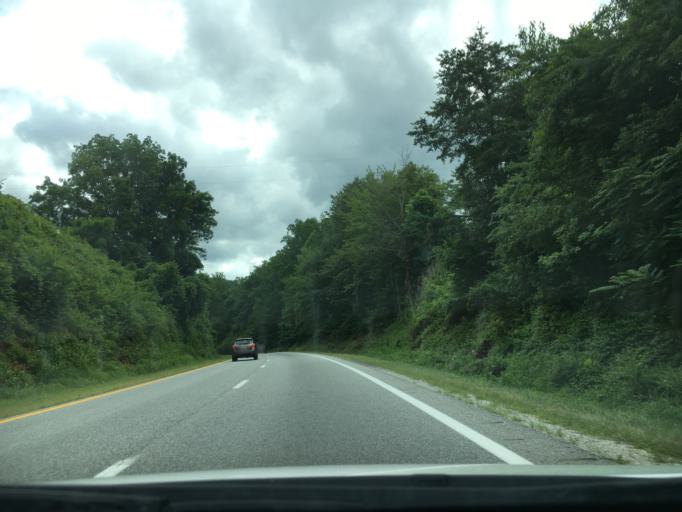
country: US
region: Virginia
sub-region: Nelson County
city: Nellysford
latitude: 37.8429
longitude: -78.7878
